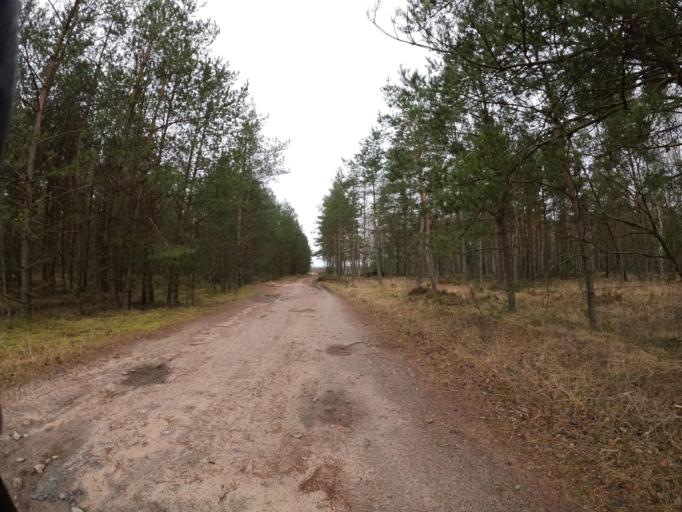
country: PL
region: Greater Poland Voivodeship
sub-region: Powiat zlotowski
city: Sypniewo
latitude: 53.5146
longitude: 16.5629
